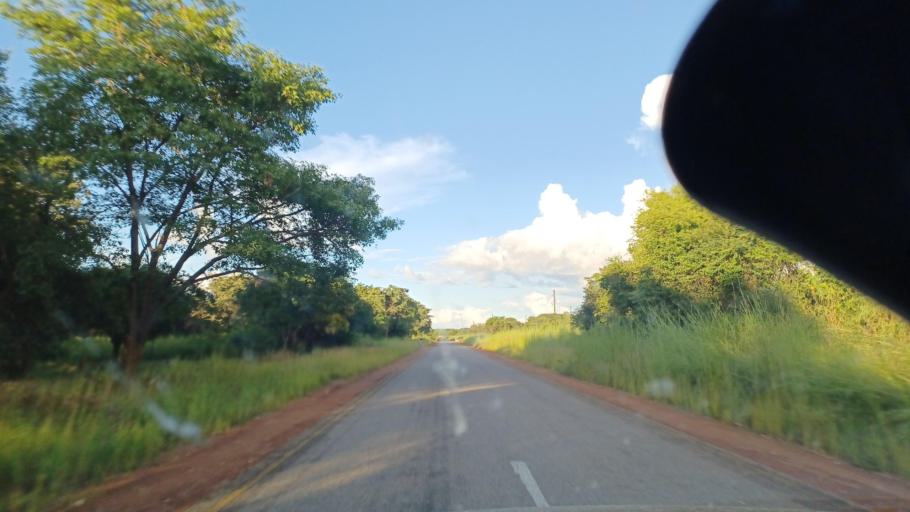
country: ZM
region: North-Western
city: Kalengwa
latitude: -13.1349
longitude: 25.1638
